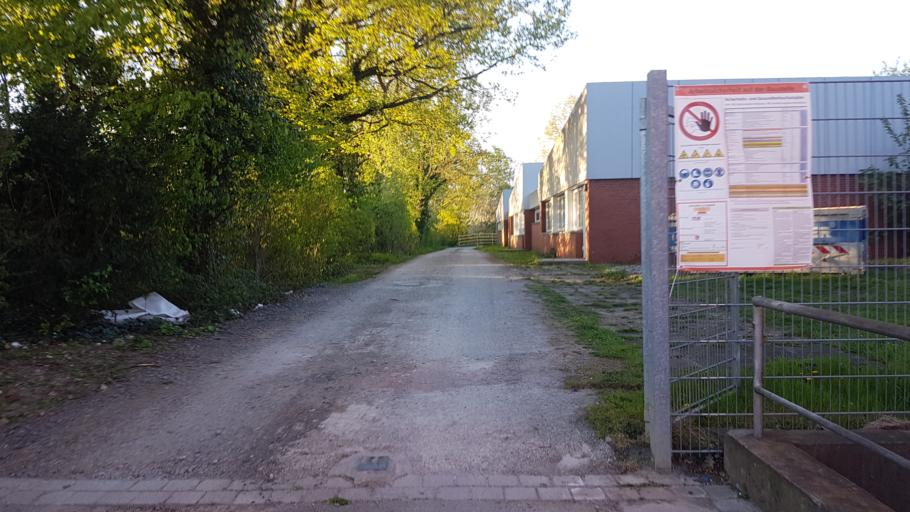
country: DE
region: Lower Saxony
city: Langenhagen
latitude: 52.4140
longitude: 9.7484
